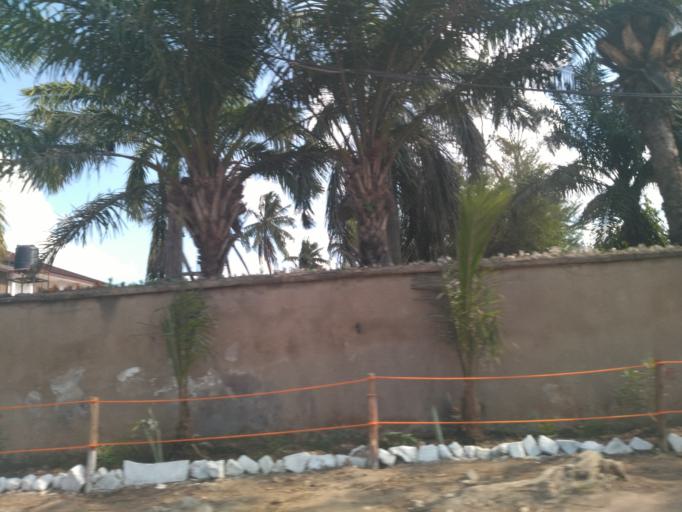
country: TZ
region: Dar es Salaam
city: Magomeni
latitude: -6.7699
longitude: 39.2615
